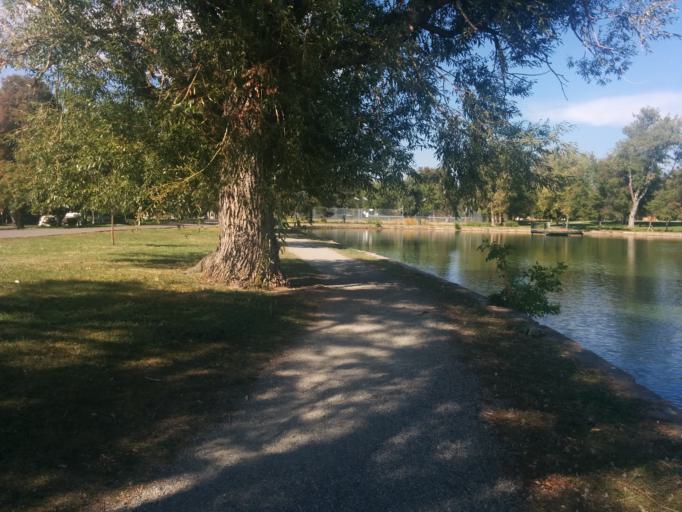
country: US
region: Colorado
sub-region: Arapahoe County
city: Glendale
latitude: 39.6967
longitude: -104.9727
